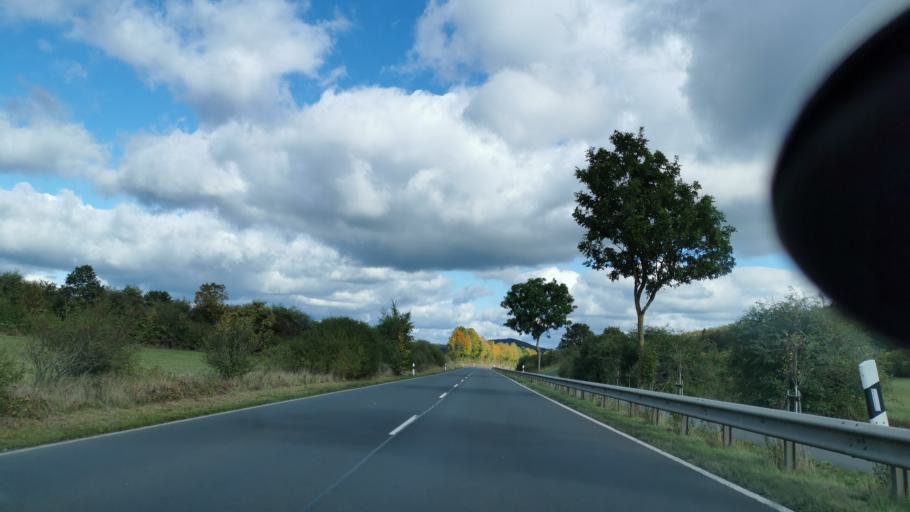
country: DE
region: Rheinland-Pfalz
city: Walsdorf
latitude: 50.2914
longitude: 6.7139
